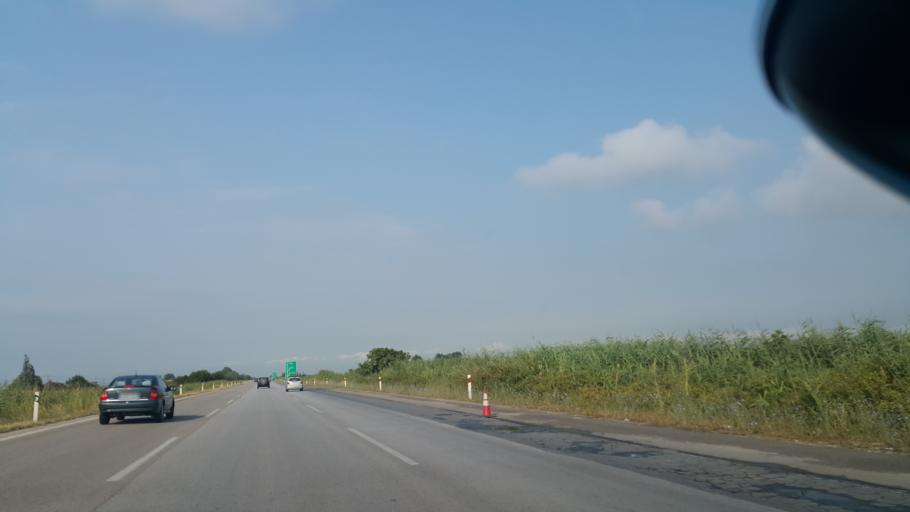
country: GR
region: Central Macedonia
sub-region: Nomos Thessalonikis
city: Chalastra
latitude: 40.6234
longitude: 22.7610
